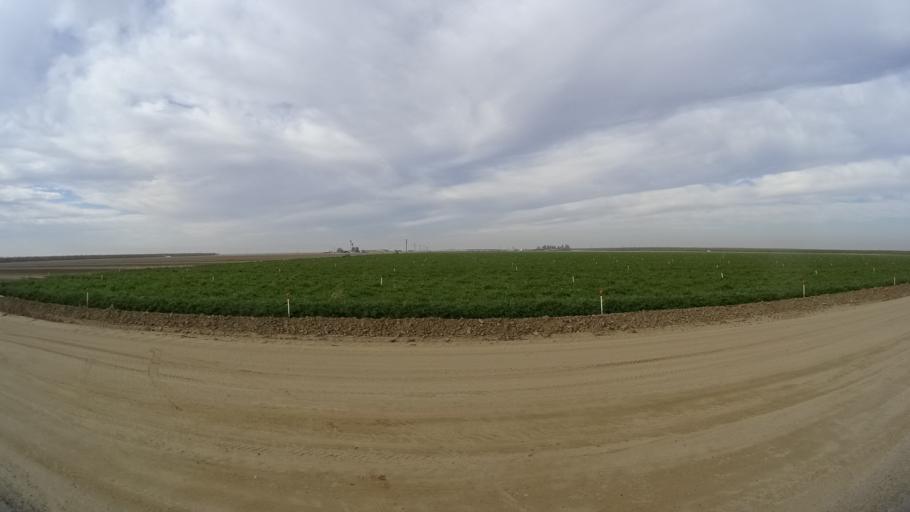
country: US
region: California
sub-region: Kern County
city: Rosedale
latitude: 35.4166
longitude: -119.1899
